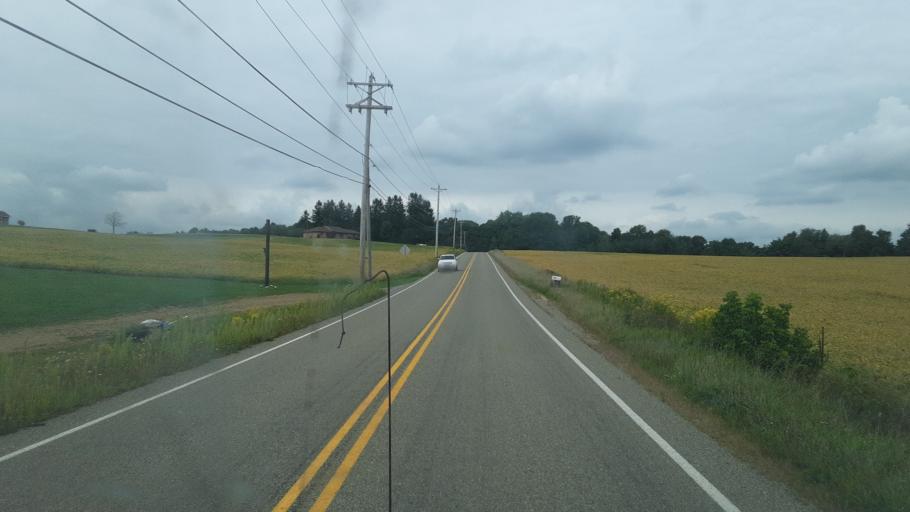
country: US
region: Pennsylvania
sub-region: Jefferson County
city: Punxsutawney
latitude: 40.9663
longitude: -79.0990
